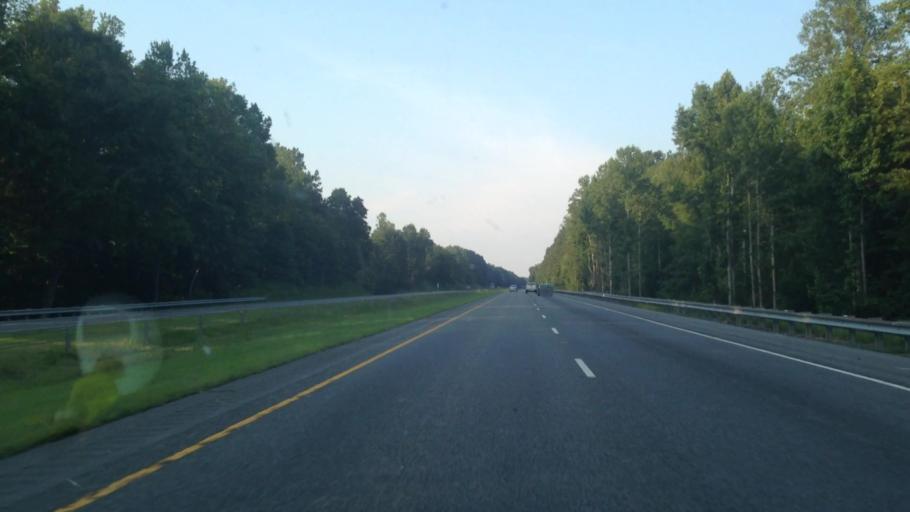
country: US
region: North Carolina
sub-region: Rockingham County
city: Reidsville
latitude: 36.4098
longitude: -79.5922
